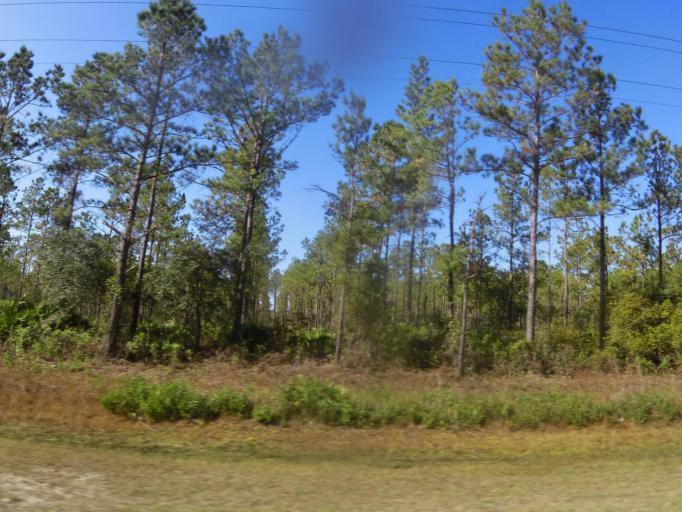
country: US
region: Georgia
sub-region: Charlton County
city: Folkston
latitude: 30.7468
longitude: -82.0709
